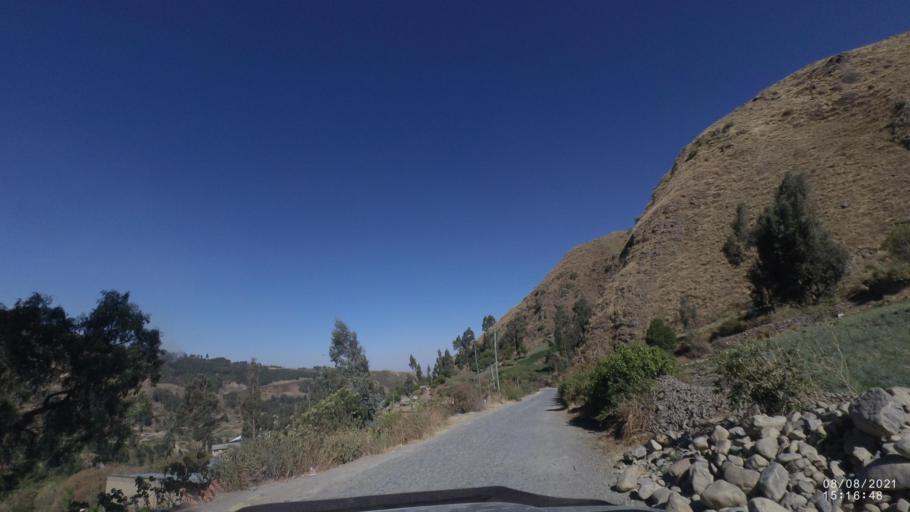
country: BO
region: Cochabamba
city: Sipe Sipe
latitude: -17.2845
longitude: -66.3063
